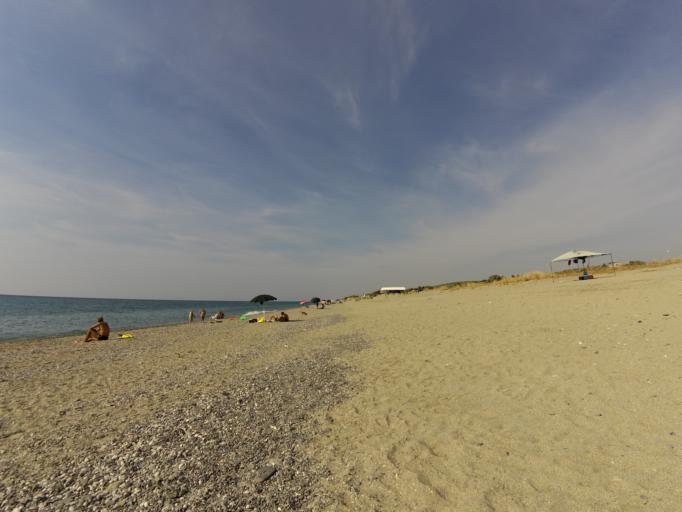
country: IT
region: Calabria
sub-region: Provincia di Reggio Calabria
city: Monasterace Marina
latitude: 38.4196
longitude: 16.5644
